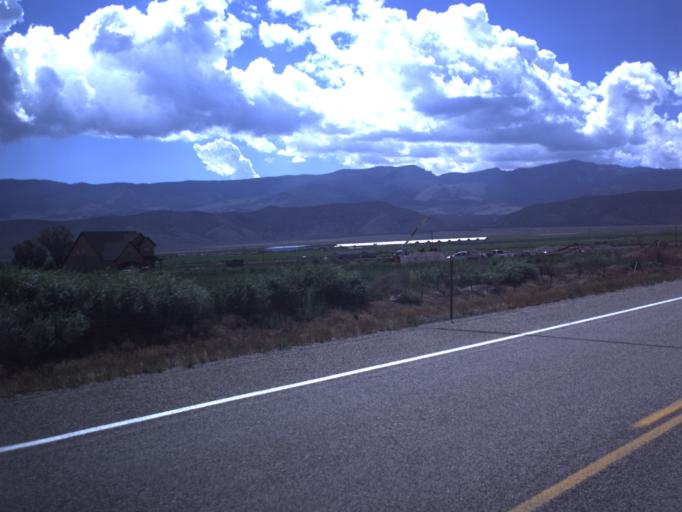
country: US
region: Utah
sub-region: Piute County
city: Junction
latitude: 38.1603
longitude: -112.2796
